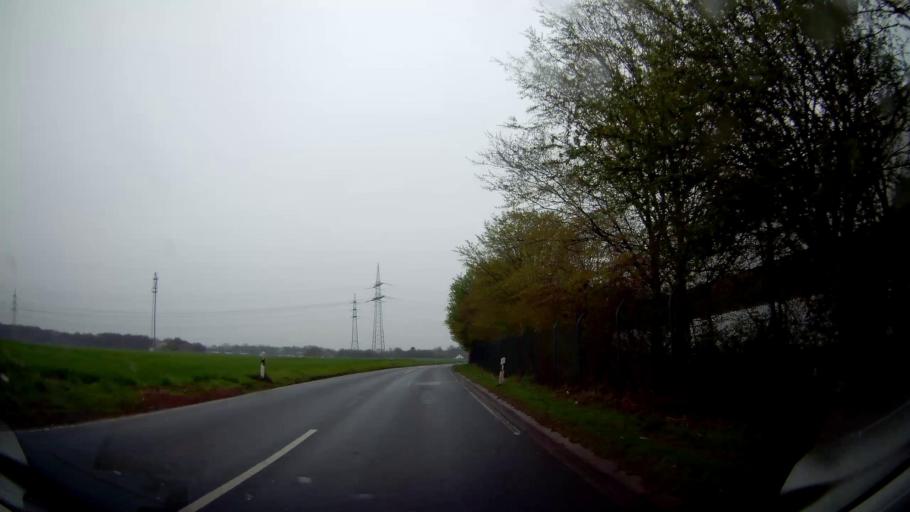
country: DE
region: North Rhine-Westphalia
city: Castrop-Rauxel
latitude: 51.5244
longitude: 7.3020
